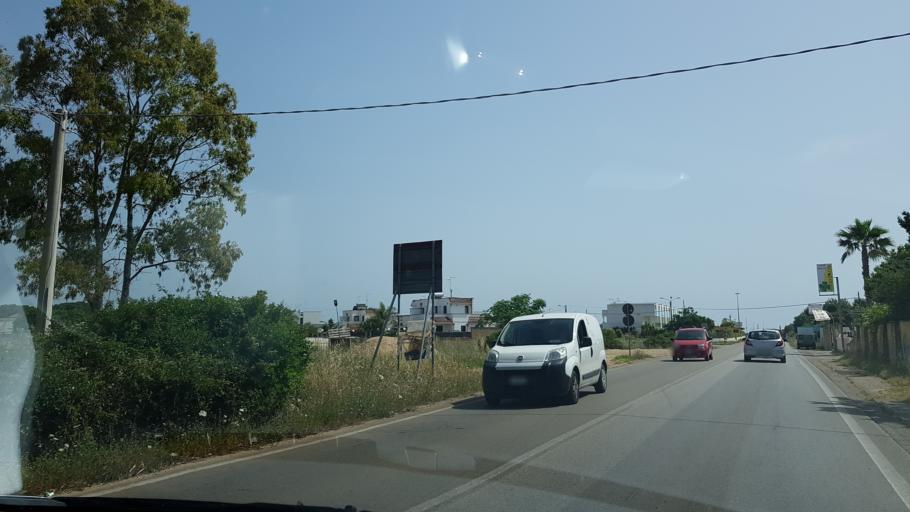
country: IT
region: Apulia
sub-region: Provincia di Lecce
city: Porto Cesareo
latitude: 40.2993
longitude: 17.8577
